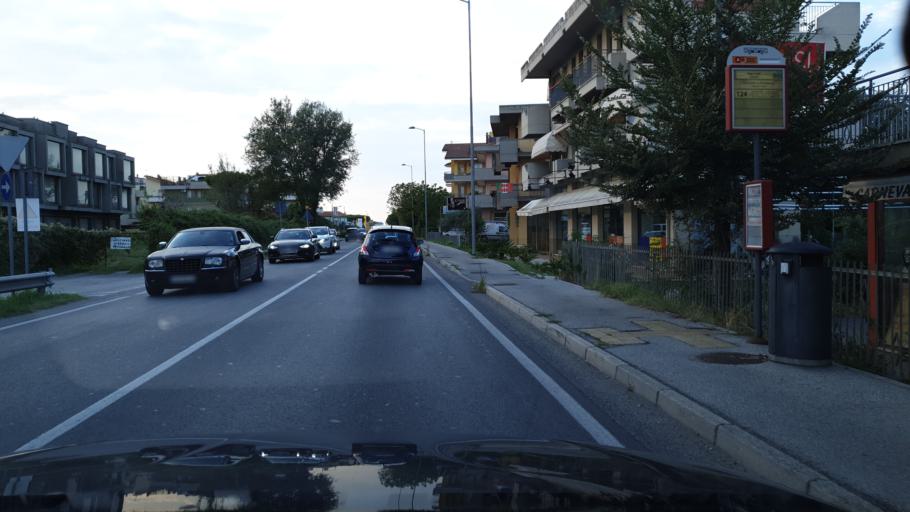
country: IT
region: Emilia-Romagna
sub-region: Provincia di Rimini
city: Rivazzurra
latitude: 44.0327
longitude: 12.6050
